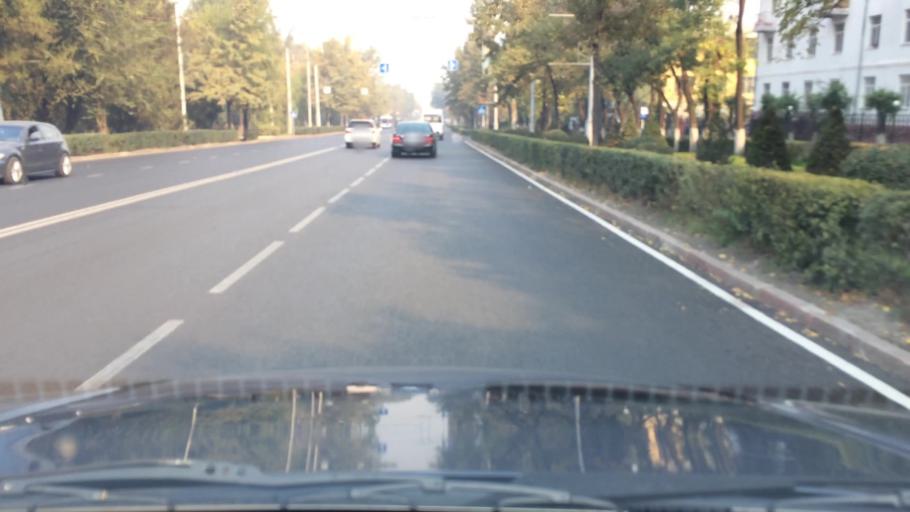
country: KG
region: Chuy
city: Bishkek
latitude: 42.8458
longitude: 74.5863
